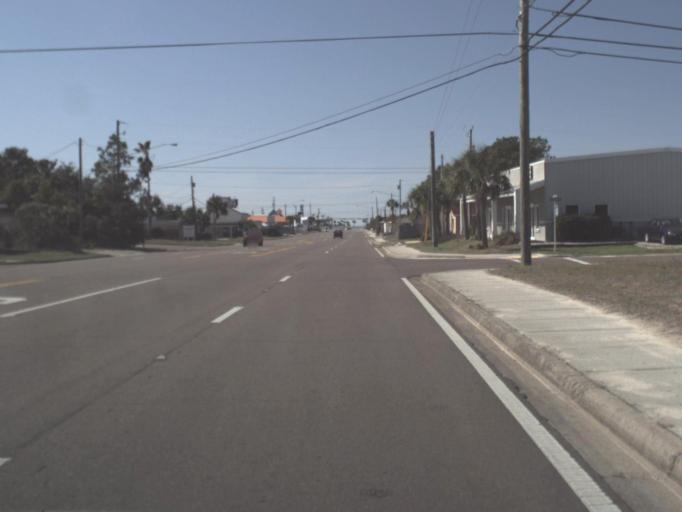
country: US
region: Florida
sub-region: Bay County
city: Panama City Beach
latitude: 30.1988
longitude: -85.8394
